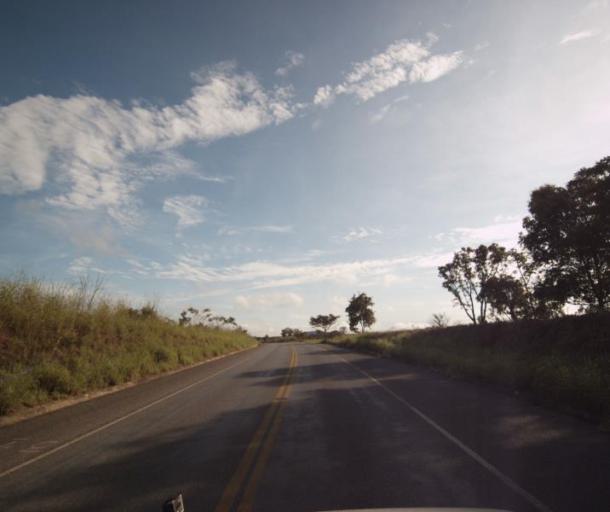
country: BR
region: Goias
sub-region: Pirenopolis
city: Pirenopolis
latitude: -15.5689
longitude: -48.6217
